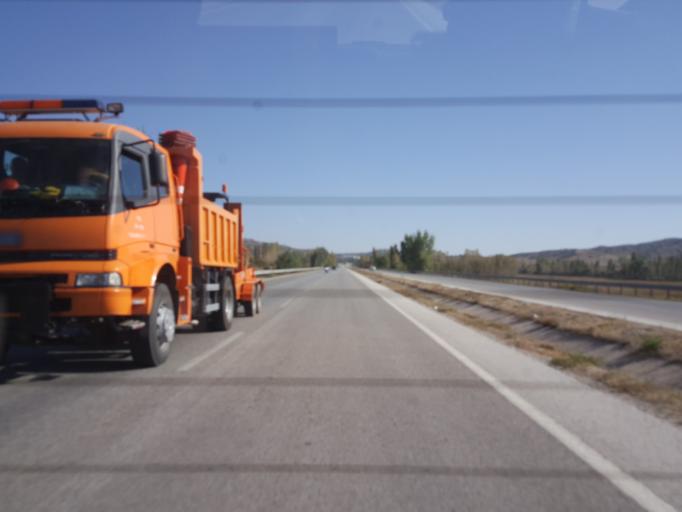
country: TR
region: Corum
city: Bogazkale
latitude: 40.2337
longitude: 34.5789
